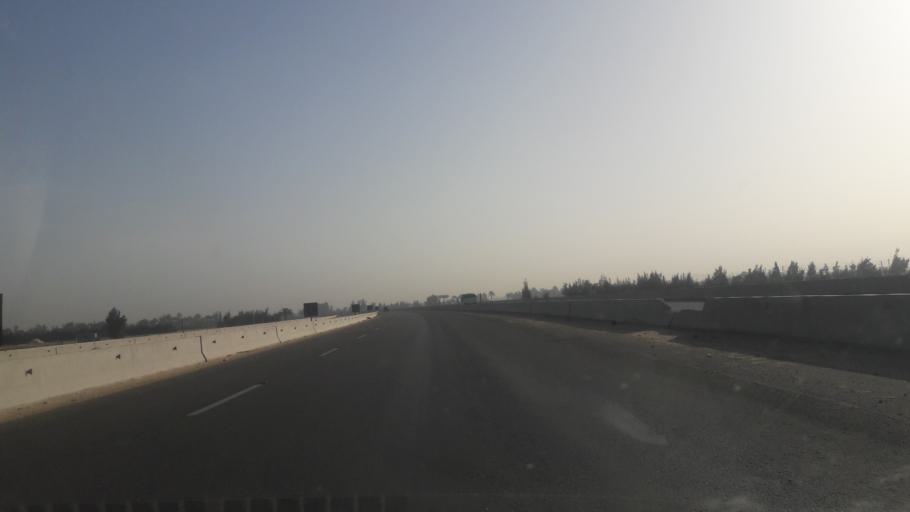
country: EG
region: Al Isma'iliyah
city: Ismailia
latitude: 30.7073
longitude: 32.1158
